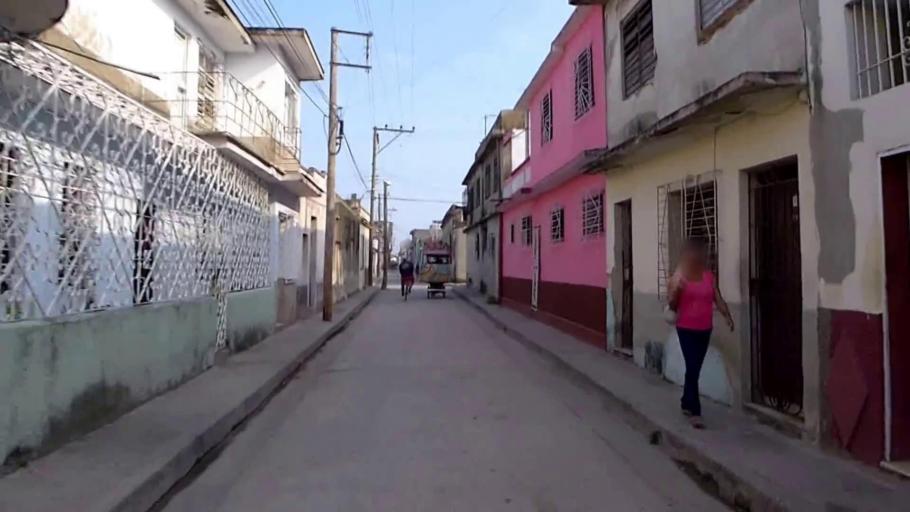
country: CU
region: Camaguey
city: Camaguey
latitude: 21.3750
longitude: -77.9200
